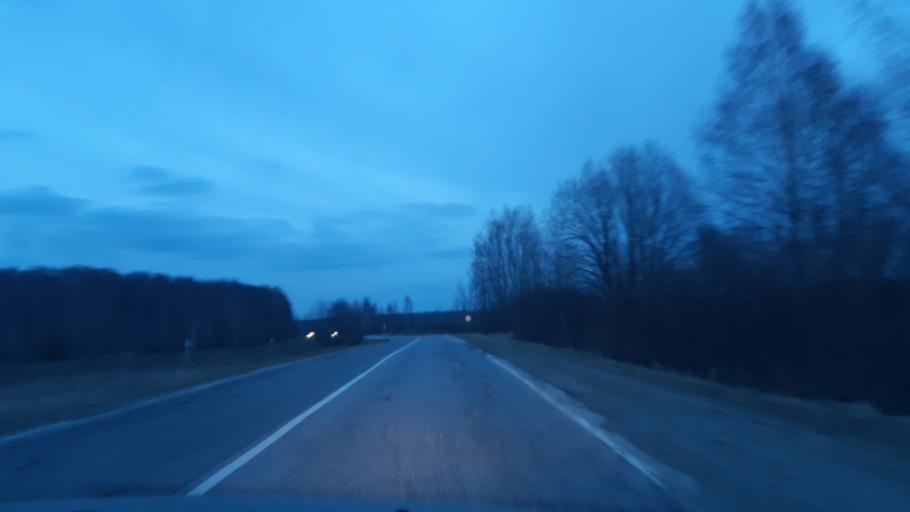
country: RU
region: Vladimir
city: Luknovo
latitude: 56.1900
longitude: 42.0251
